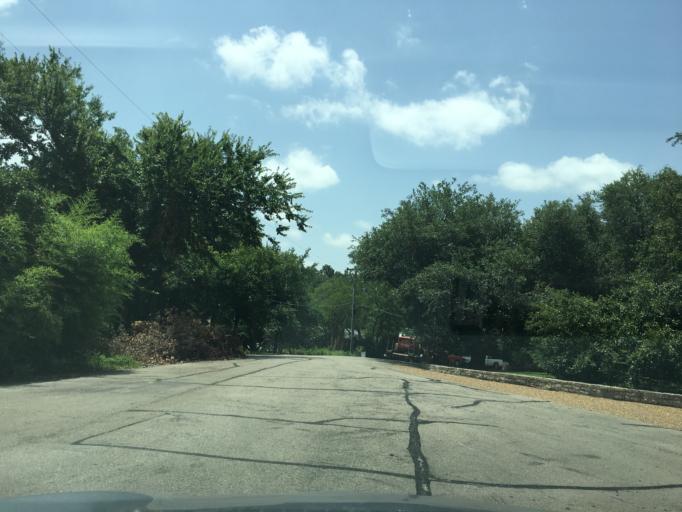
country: US
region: Texas
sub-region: Dallas County
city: University Park
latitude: 32.9076
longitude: -96.7887
